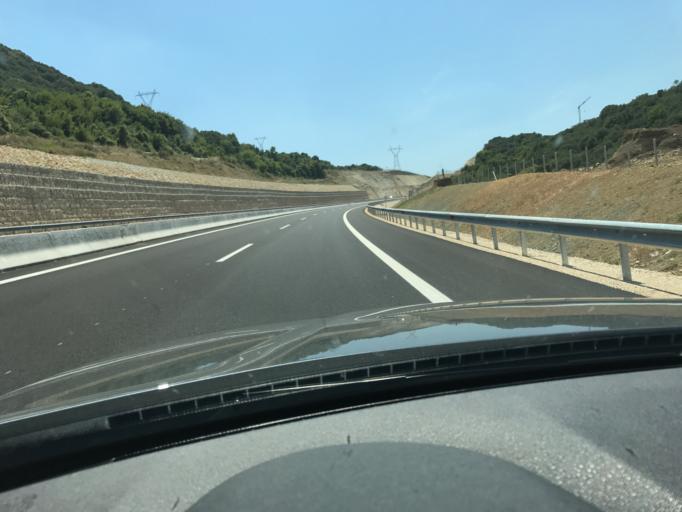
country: GR
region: Epirus
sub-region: Nomos Ioanninon
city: Agia Kyriaki
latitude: 39.5037
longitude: 20.8903
